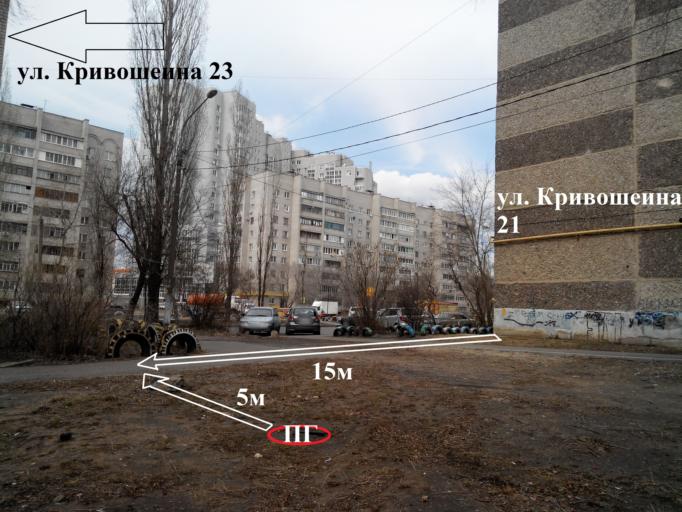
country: RU
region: Voronezj
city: Voronezh
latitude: 51.6413
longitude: 39.1459
